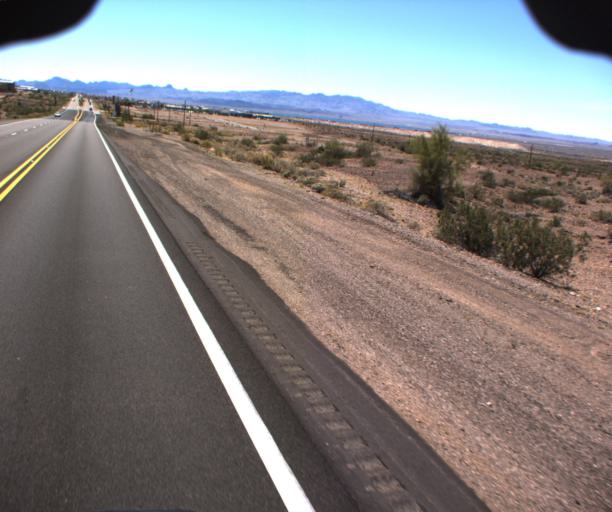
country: US
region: Arizona
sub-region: Mohave County
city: Desert Hills
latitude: 34.5835
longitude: -114.3684
